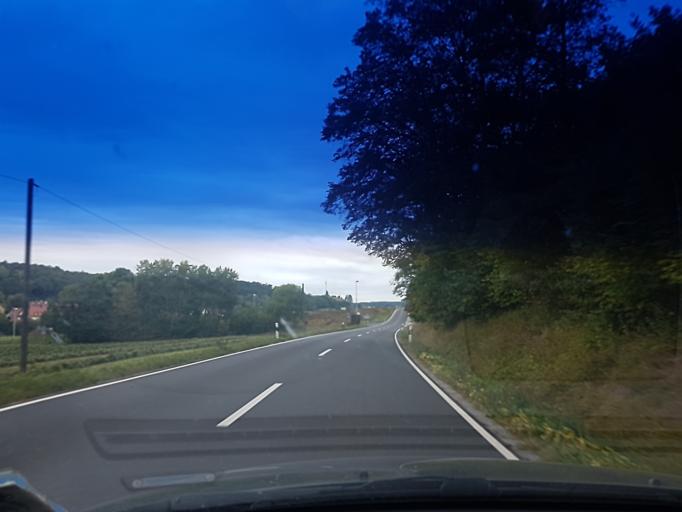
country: DE
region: Bavaria
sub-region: Upper Franconia
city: Burgwindheim
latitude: 49.8396
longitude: 10.5244
